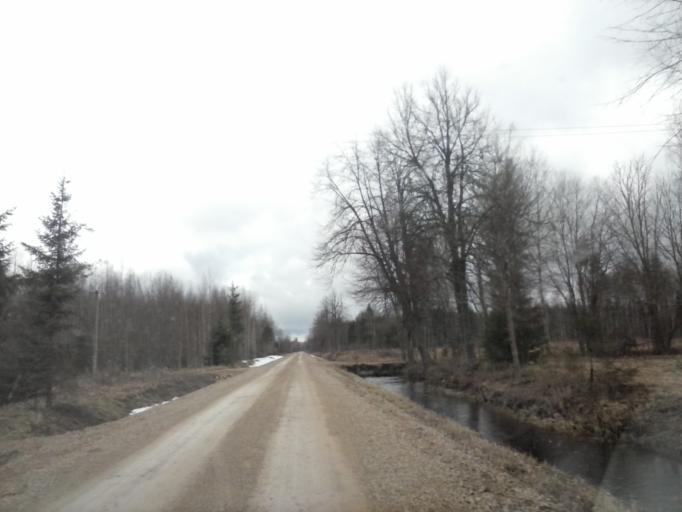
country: EE
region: Jogevamaa
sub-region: Mustvee linn
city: Mustvee
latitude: 59.0946
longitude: 26.8439
